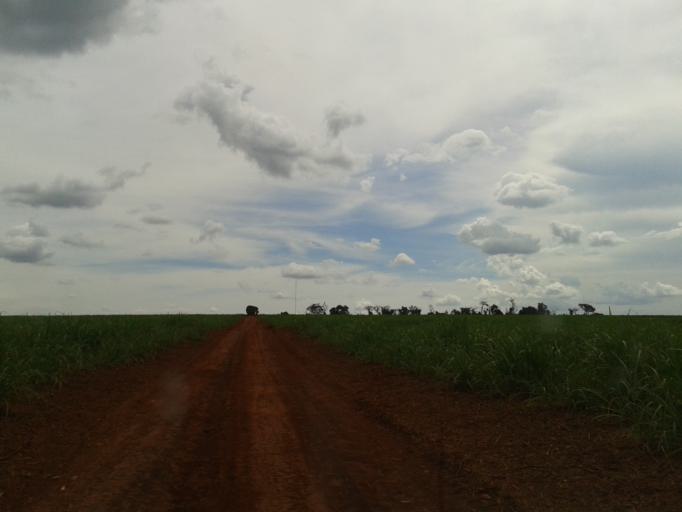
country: BR
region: Minas Gerais
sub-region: Centralina
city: Centralina
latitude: -18.6632
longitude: -49.2569
